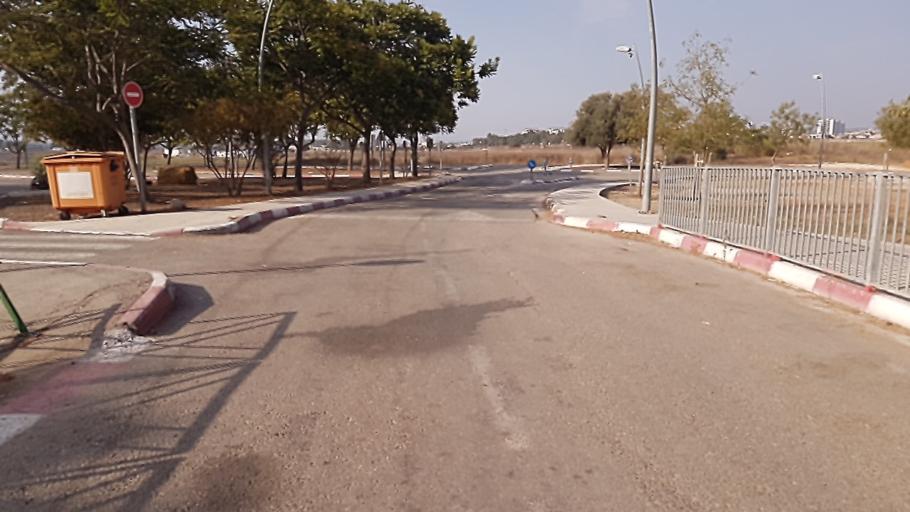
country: IL
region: Central District
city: Rosh Ha'Ayin
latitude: 32.0853
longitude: 34.9377
